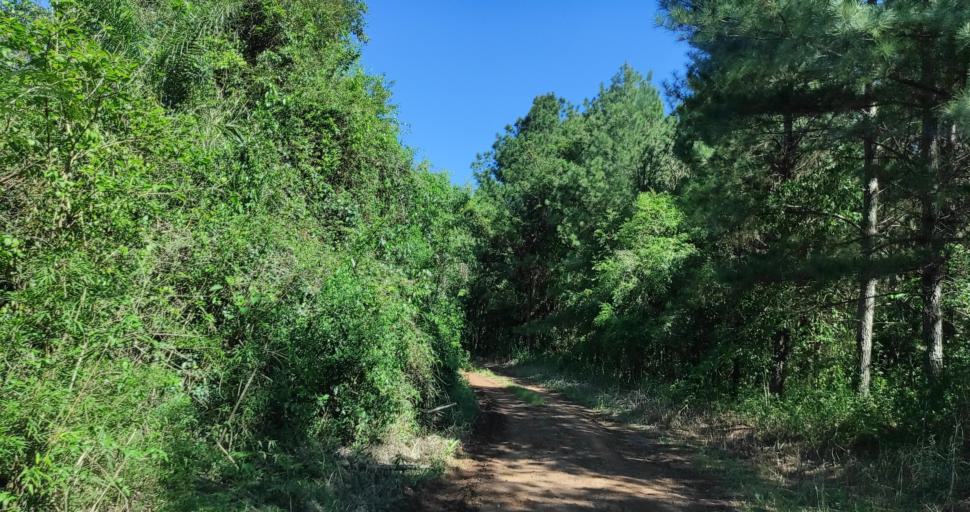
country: AR
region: Misiones
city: Ruiz de Montoya
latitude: -26.9516
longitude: -54.9813
